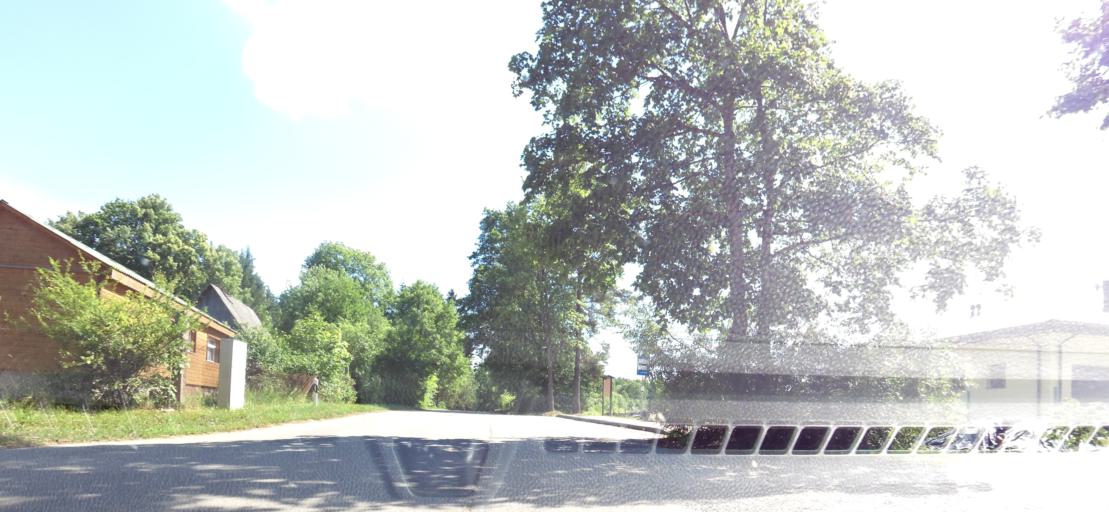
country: LT
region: Vilnius County
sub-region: Vilnius
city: Fabijoniskes
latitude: 54.8150
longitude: 25.3218
